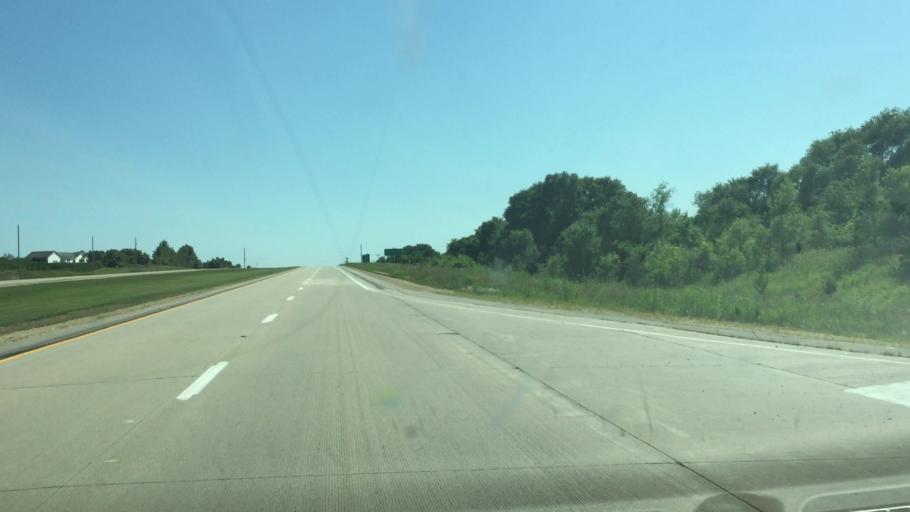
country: US
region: Iowa
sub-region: Jones County
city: Monticello
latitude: 42.2560
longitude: -91.1570
